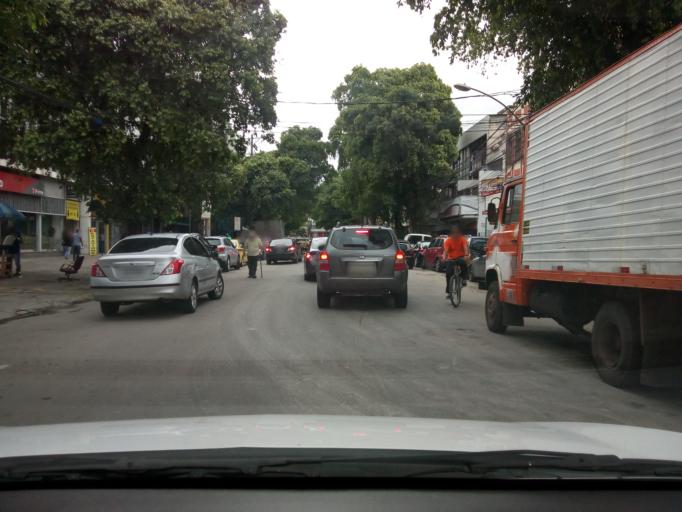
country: BR
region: Rio de Janeiro
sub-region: Rio De Janeiro
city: Rio de Janeiro
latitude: -22.9018
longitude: -43.2174
